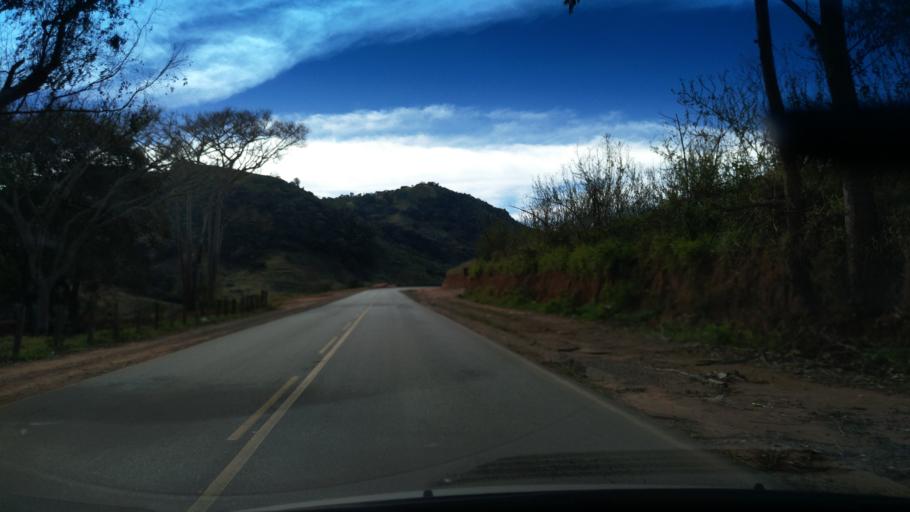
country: BR
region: Minas Gerais
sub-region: Andradas
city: Andradas
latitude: -22.0580
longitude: -46.4319
